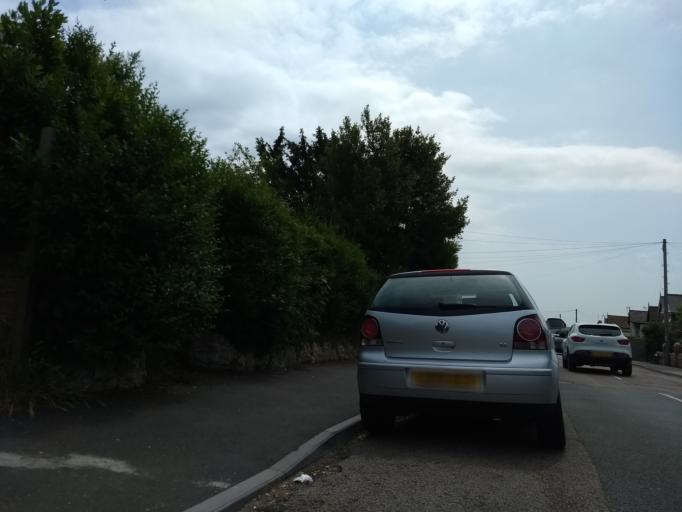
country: GB
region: England
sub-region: Isle of Wight
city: Ryde
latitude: 50.7180
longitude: -1.1496
